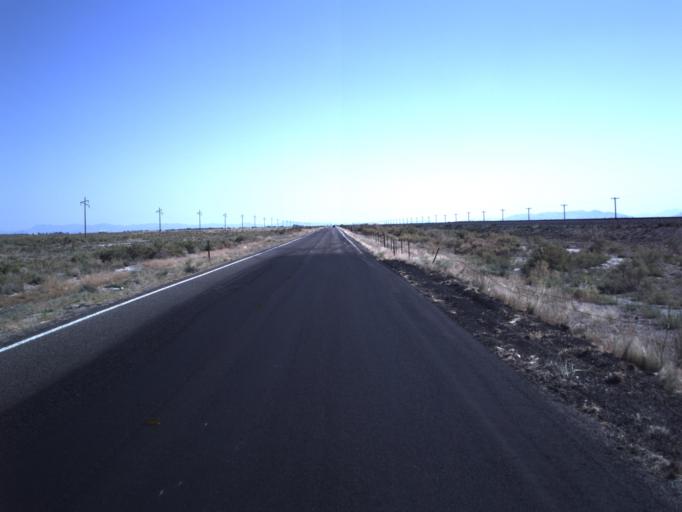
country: US
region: Utah
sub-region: Millard County
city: Delta
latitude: 39.2027
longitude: -112.6864
